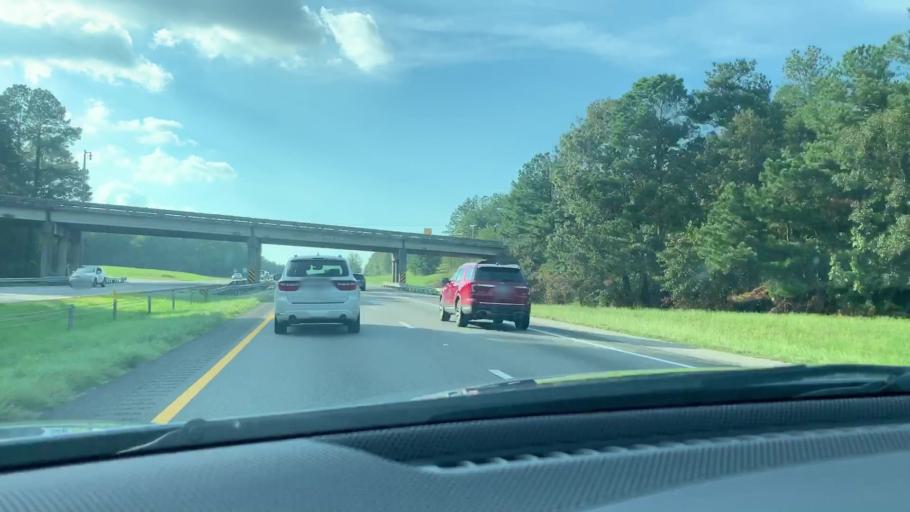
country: US
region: South Carolina
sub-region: Calhoun County
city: Oak Grove
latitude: 33.7646
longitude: -80.9633
